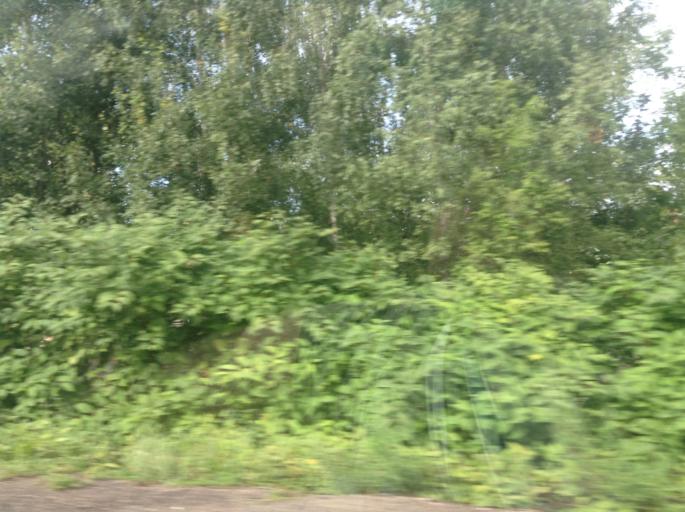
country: RU
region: Moskovskaya
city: Yegor'yevsk
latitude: 55.3617
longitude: 39.1011
